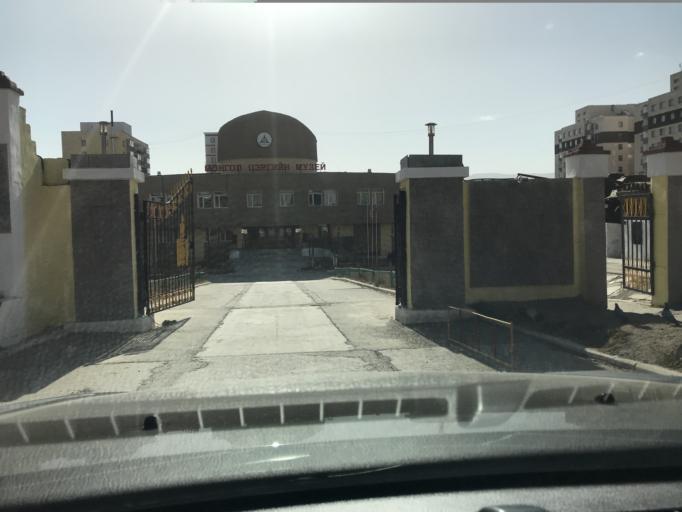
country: MN
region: Ulaanbaatar
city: Ulaanbaatar
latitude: 47.9233
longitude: 106.9533
